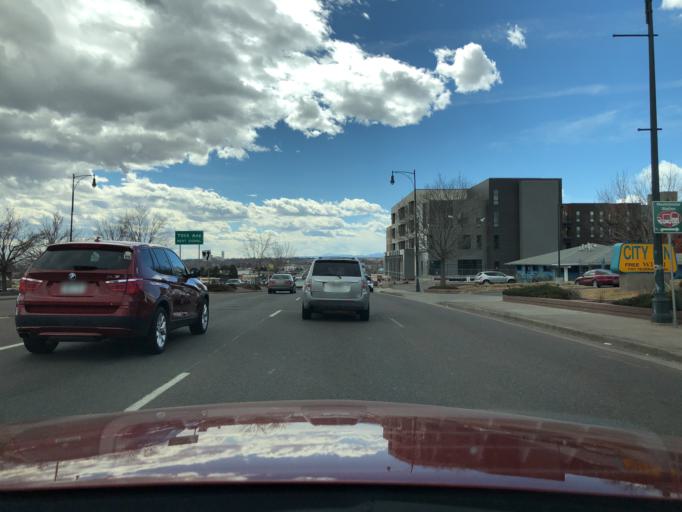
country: US
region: Colorado
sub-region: Adams County
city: Westminster
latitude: 39.8261
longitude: -105.0249
